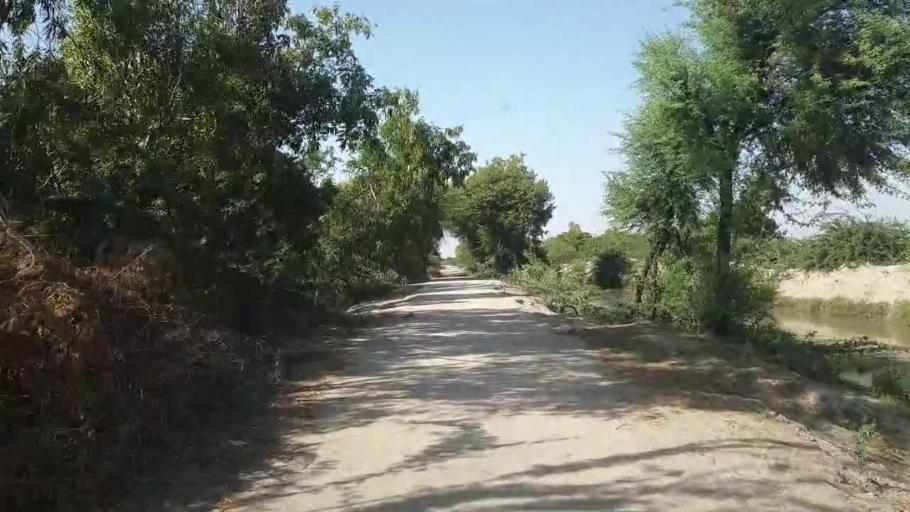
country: PK
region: Sindh
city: Kadhan
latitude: 24.5705
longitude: 68.9883
